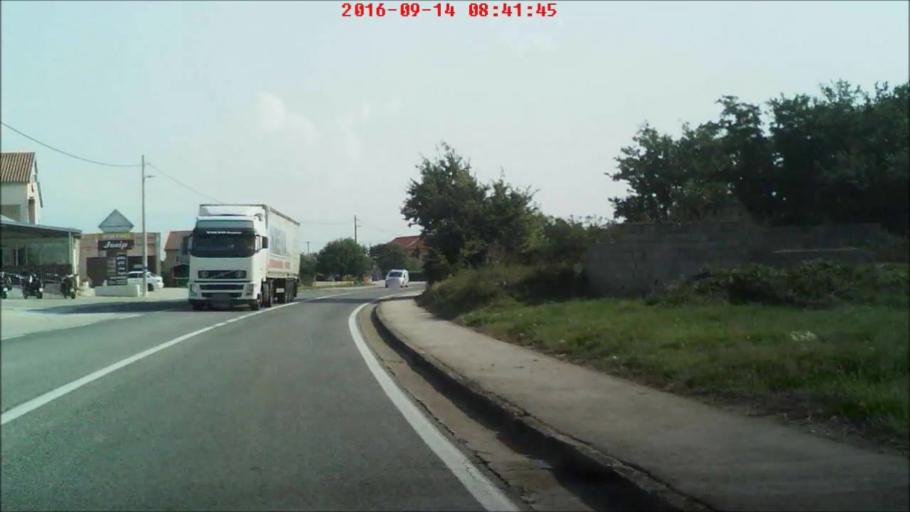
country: HR
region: Zadarska
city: Policnik
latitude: 44.1879
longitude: 15.3979
